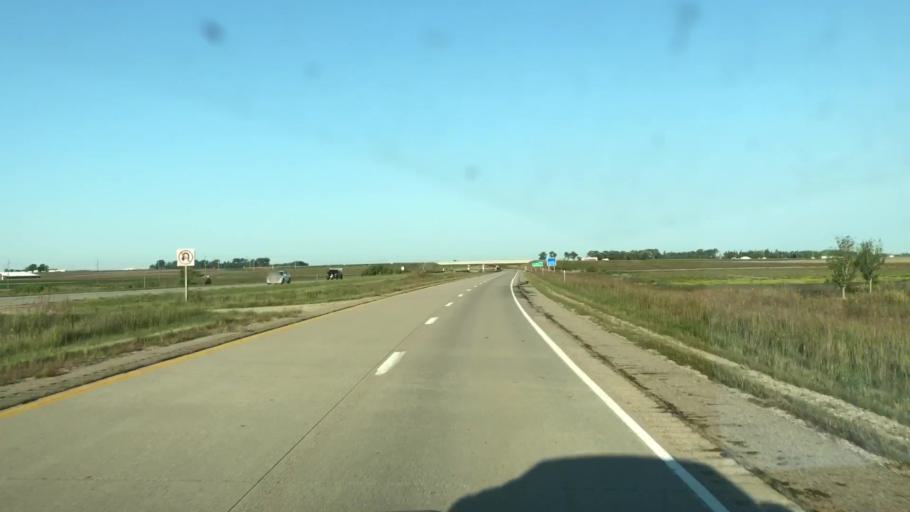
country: US
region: Iowa
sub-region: Osceola County
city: Sibley
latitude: 43.3846
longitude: -95.7325
